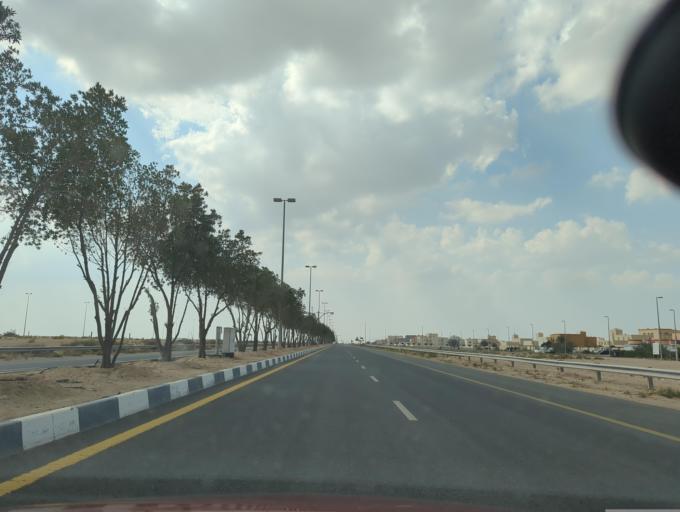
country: AE
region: Abu Dhabi
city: Abu Dhabi
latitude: 24.3645
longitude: 54.7199
